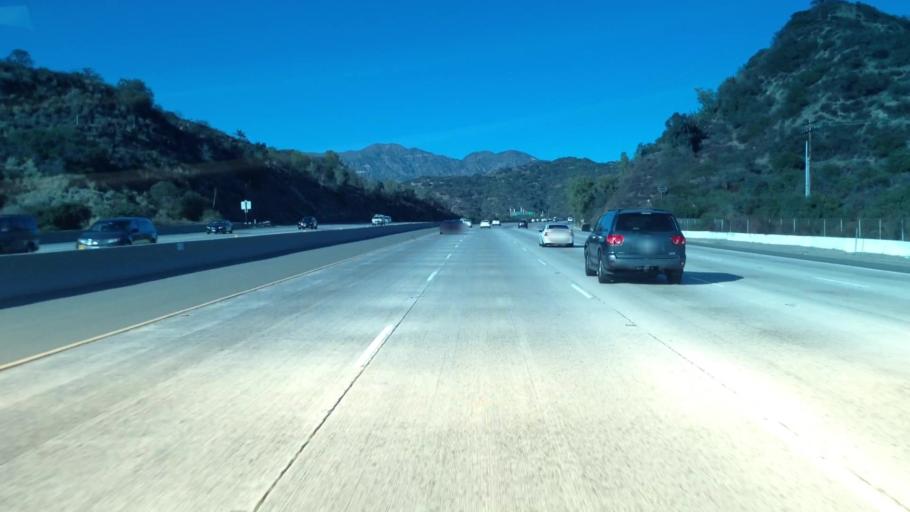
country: US
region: California
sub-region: Los Angeles County
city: La Canada Flintridge
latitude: 34.1774
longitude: -118.2209
